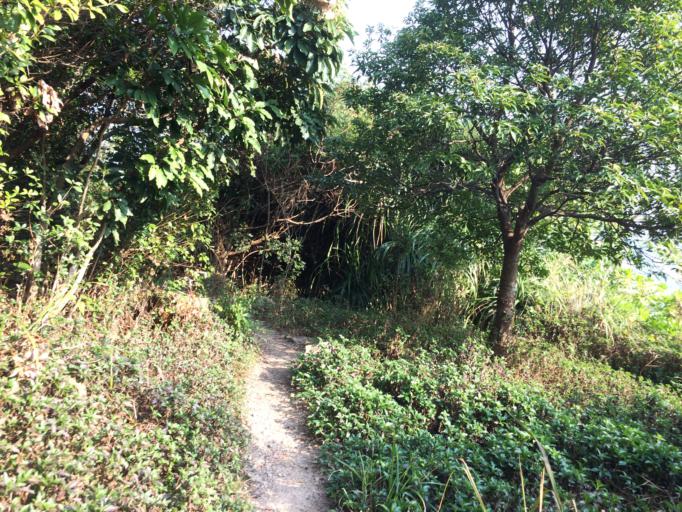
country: HK
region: Tai Po
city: Tai Po
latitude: 22.4509
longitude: 114.2289
